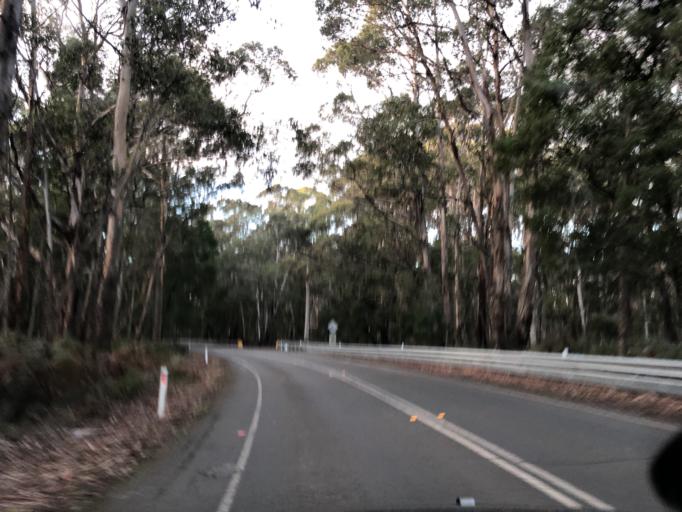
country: AU
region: Victoria
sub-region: Moorabool
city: Bacchus Marsh
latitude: -37.4108
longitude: 144.3134
